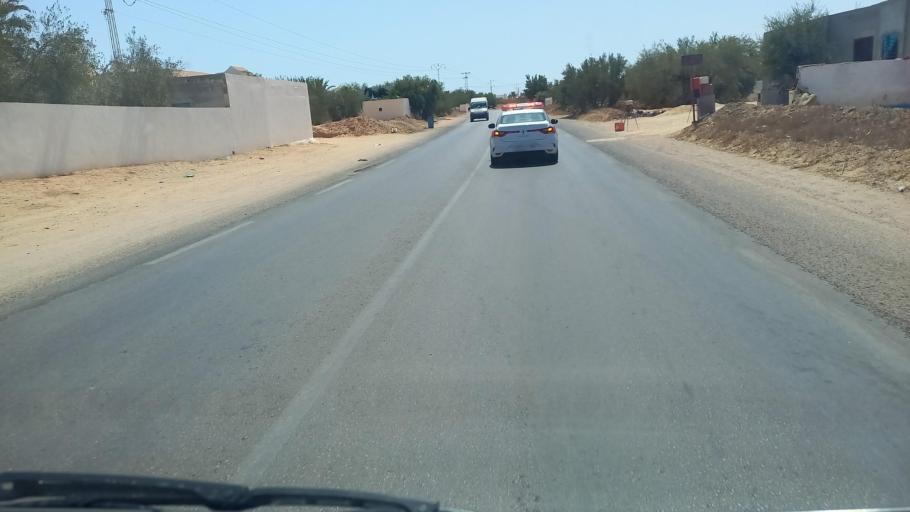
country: TN
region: Madanin
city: Midoun
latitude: 33.7682
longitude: 10.9018
